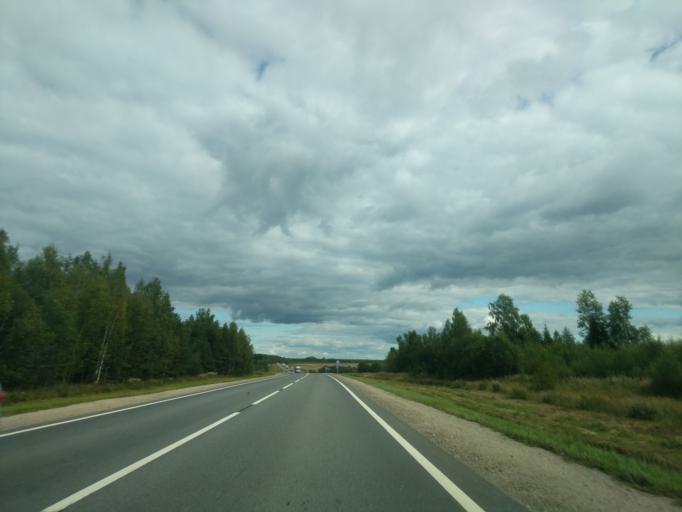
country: RU
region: Kostroma
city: Sudislavl'
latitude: 57.8181
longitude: 41.9388
